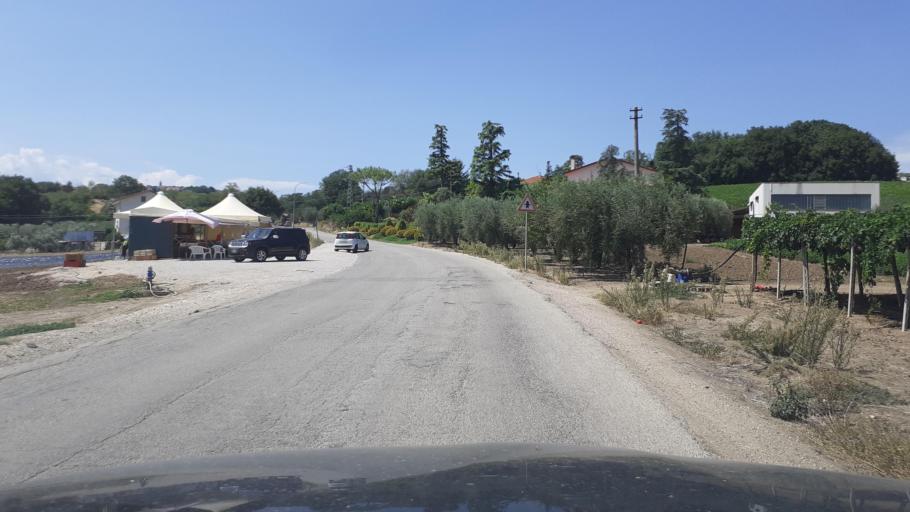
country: IT
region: Abruzzo
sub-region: Provincia di Chieti
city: Santa Maria Imbaro
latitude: 42.2154
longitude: 14.4648
